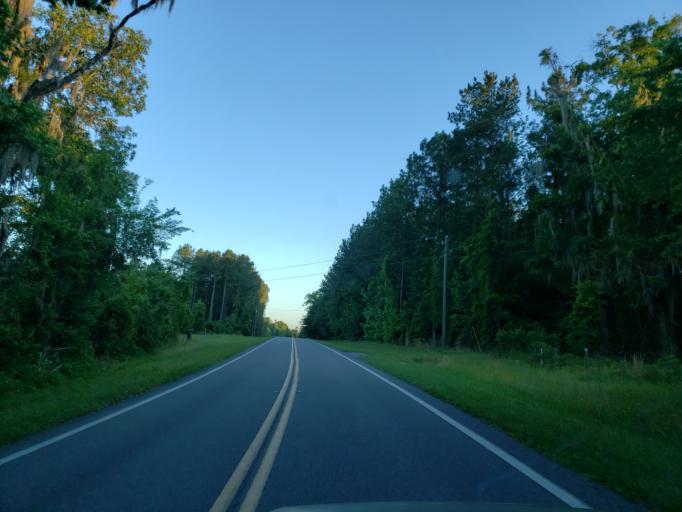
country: US
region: Florida
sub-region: Madison County
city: Madison
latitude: 30.6143
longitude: -83.2556
